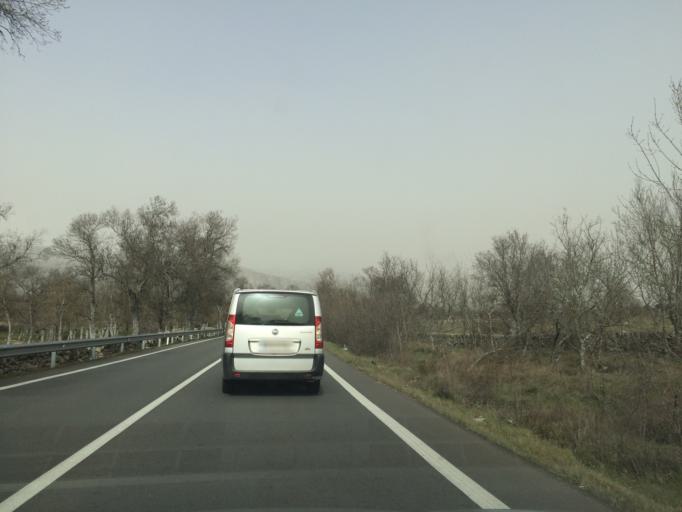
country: ES
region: Madrid
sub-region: Provincia de Madrid
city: Moralzarzal
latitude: 40.6848
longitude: -3.9546
